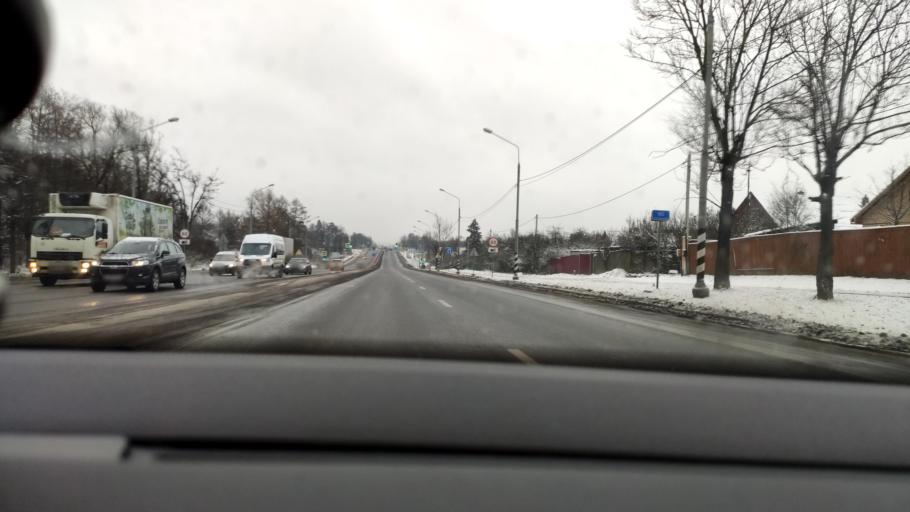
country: RU
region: Moskovskaya
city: Solnechnogorsk
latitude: 56.1582
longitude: 37.0241
